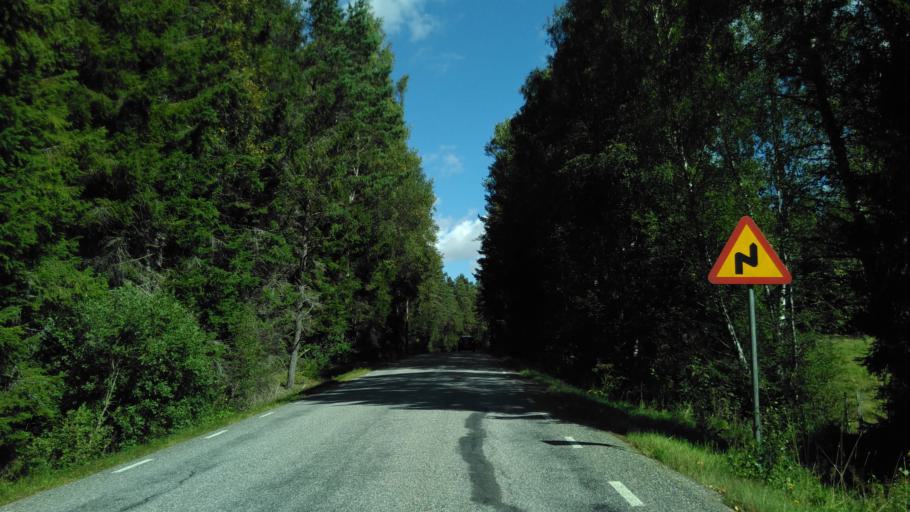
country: SE
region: Vaestra Goetaland
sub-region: Herrljunga Kommun
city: Herrljunga
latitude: 58.0938
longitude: 13.0503
